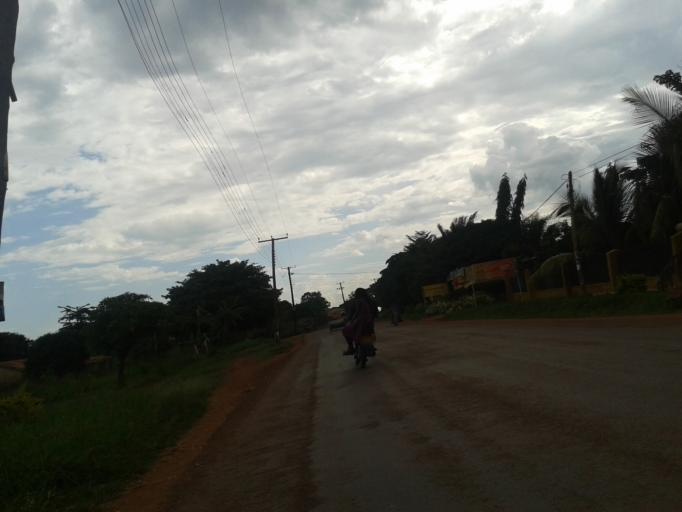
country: UG
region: Northern Region
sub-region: Gulu District
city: Gulu
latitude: 2.7795
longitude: 32.3008
